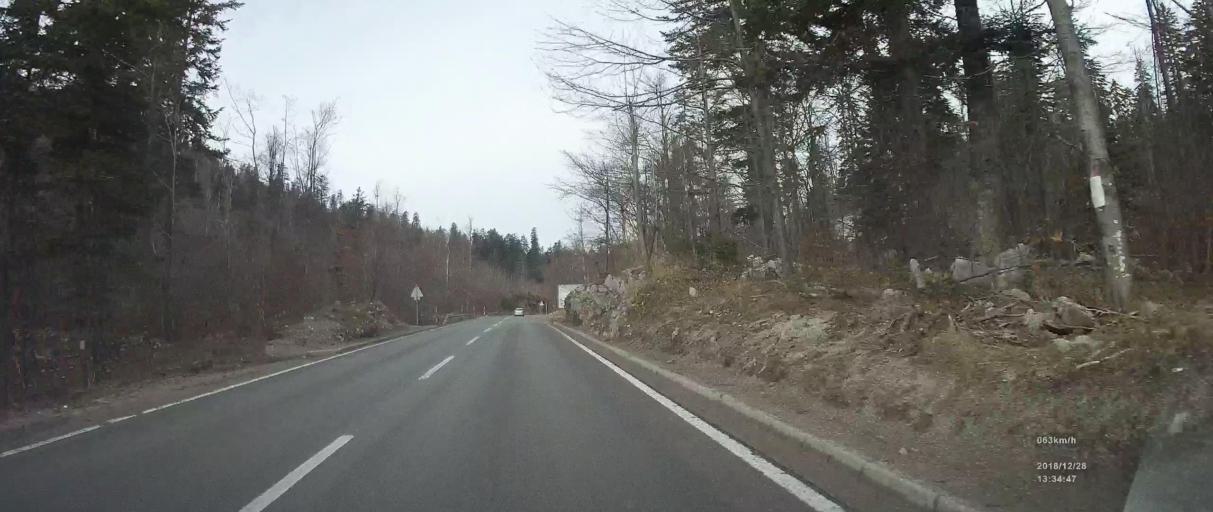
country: HR
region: Primorsko-Goranska
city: Hreljin
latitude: 45.3437
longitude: 14.6904
